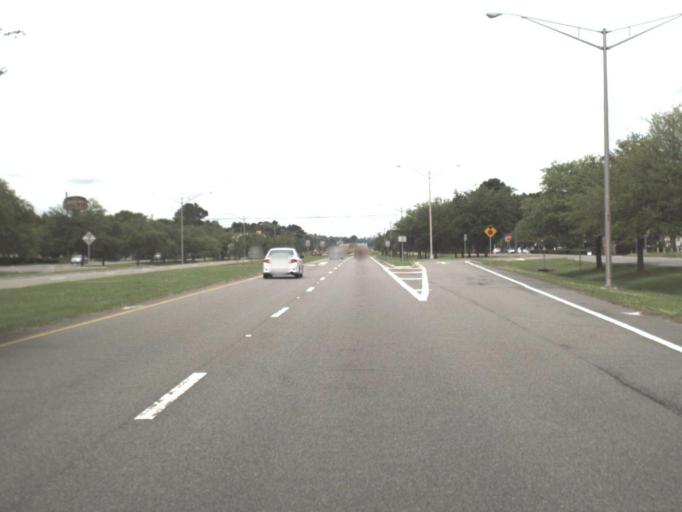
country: US
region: Florida
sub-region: Duval County
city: Jacksonville
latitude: 30.4827
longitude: -81.6502
